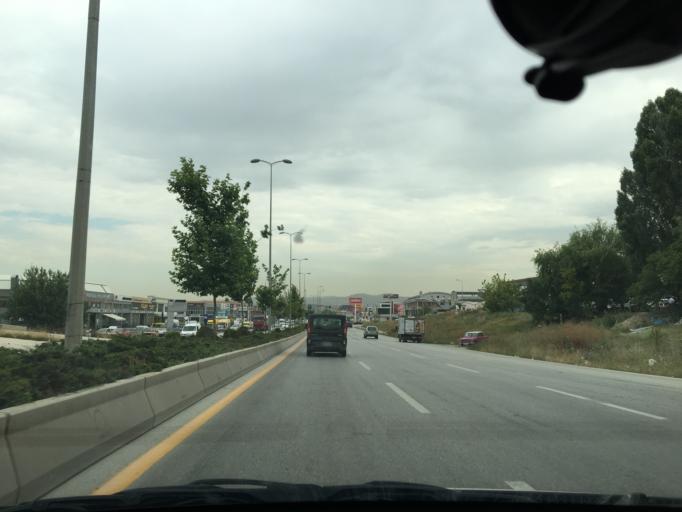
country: TR
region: Ankara
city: Batikent
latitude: 39.9308
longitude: 32.7124
